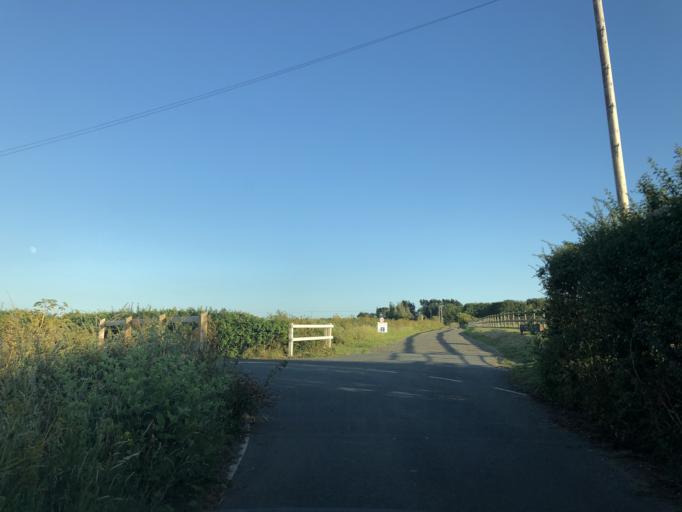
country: GB
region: England
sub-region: Isle of Wight
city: Chale
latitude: 50.6303
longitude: -1.3769
